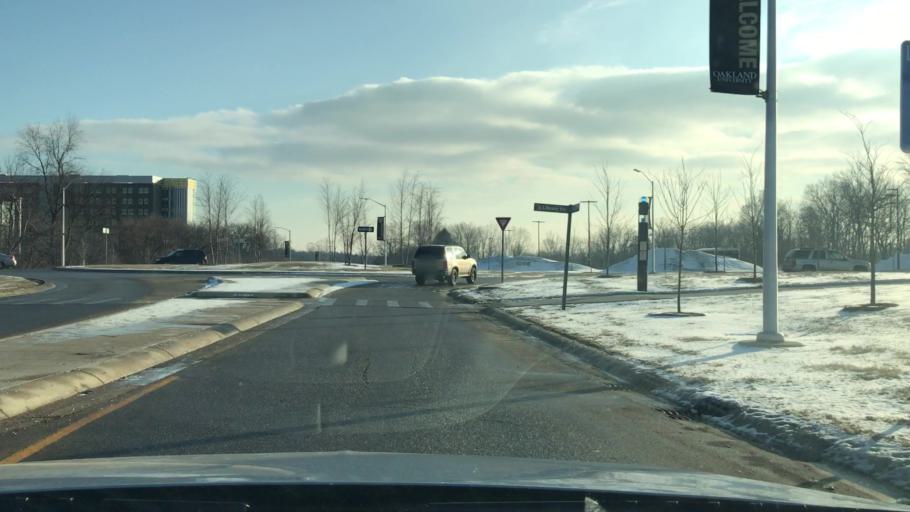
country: US
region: Michigan
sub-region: Oakland County
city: Auburn Hills
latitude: 42.6687
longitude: -83.2165
